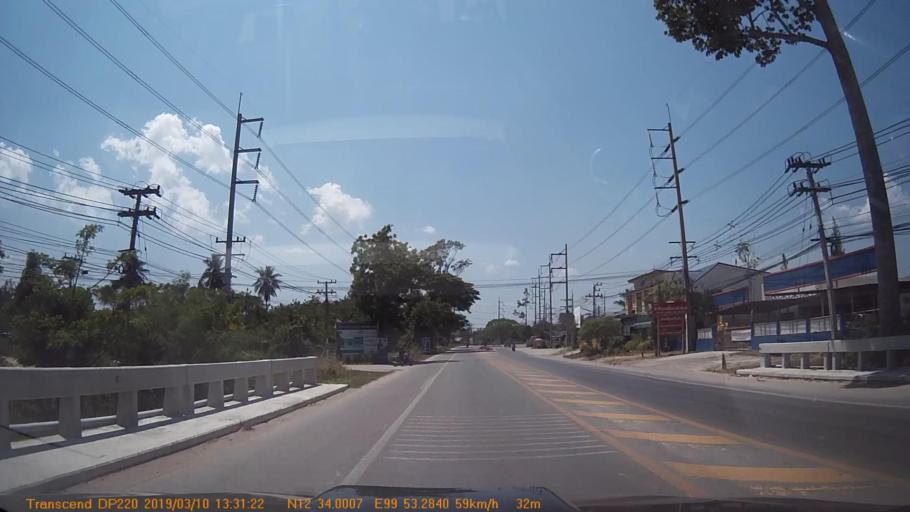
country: TH
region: Prachuap Khiri Khan
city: Hua Hin
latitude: 12.5666
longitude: 99.8878
